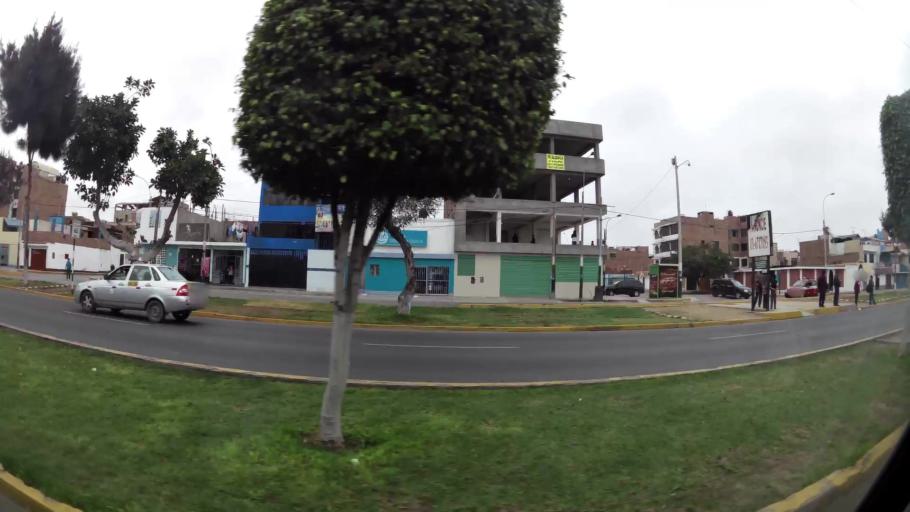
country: PE
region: Callao
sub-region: Callao
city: Callao
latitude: -12.0564
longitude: -77.1124
